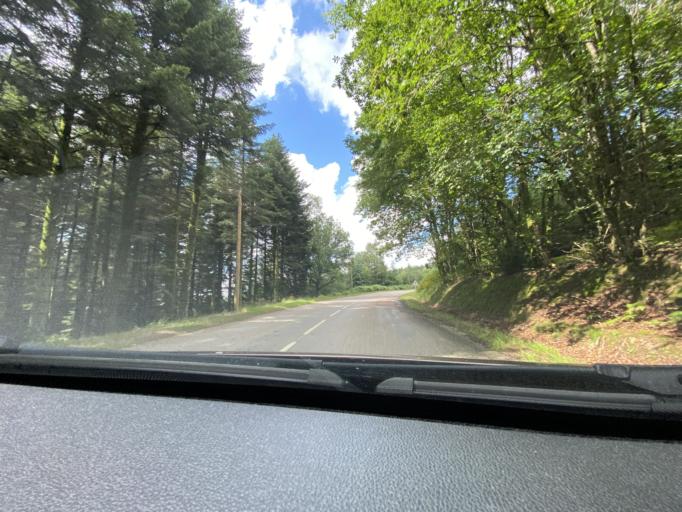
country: FR
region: Bourgogne
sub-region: Departement de la Cote-d'Or
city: Saulieu
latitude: 47.2589
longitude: 4.0706
